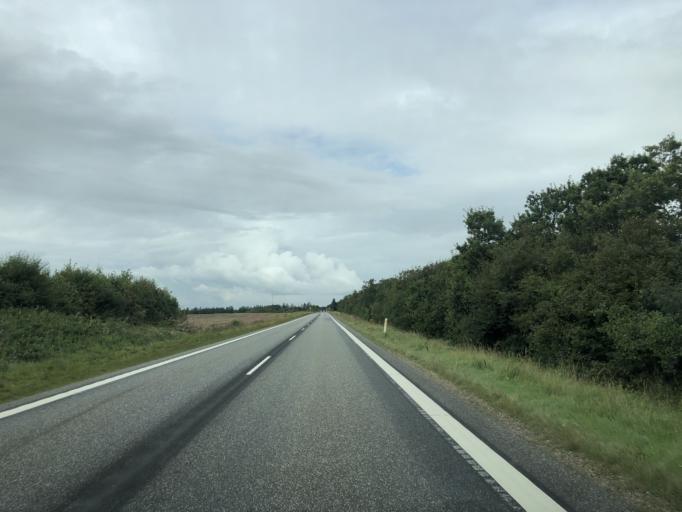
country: DK
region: Central Jutland
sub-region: Ringkobing-Skjern Kommune
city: Tarm
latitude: 55.8280
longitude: 8.4927
